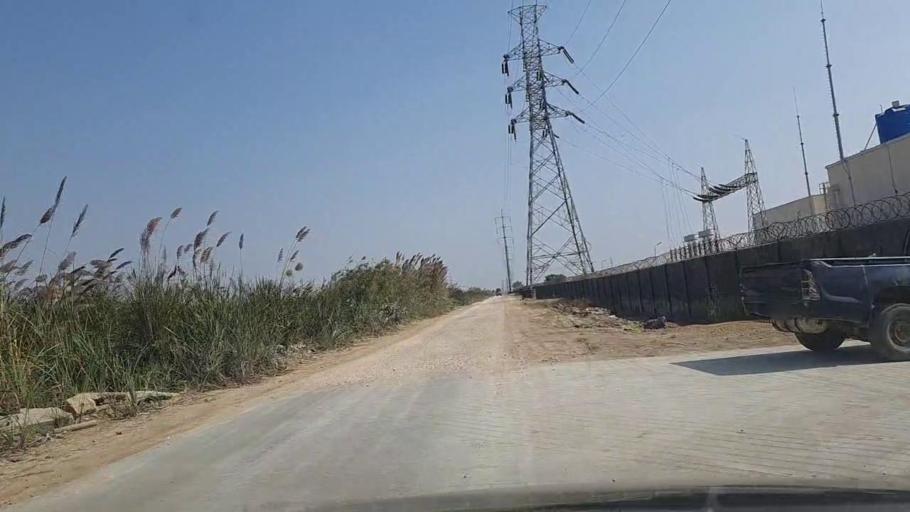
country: PK
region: Sindh
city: Gharo
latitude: 24.7218
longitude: 67.5356
